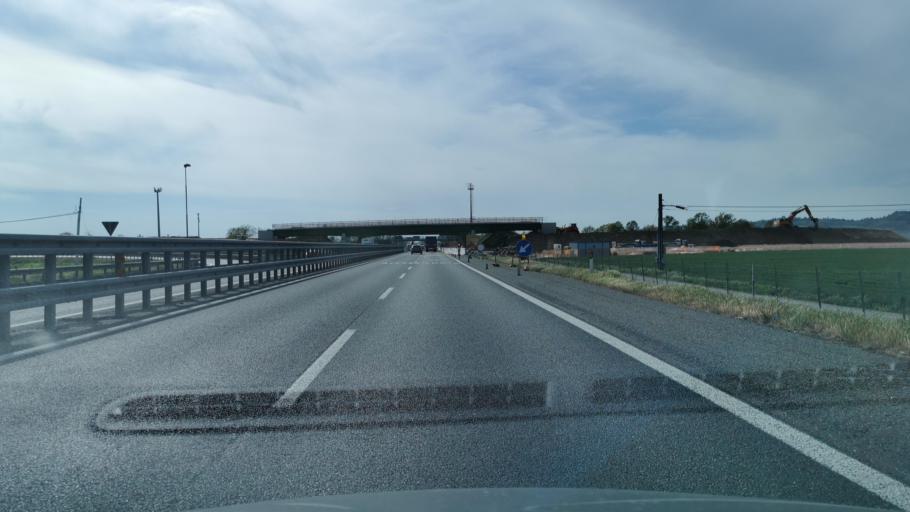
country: IT
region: Piedmont
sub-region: Provincia di Alessandria
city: Castelceriolo
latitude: 44.9251
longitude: 8.7045
